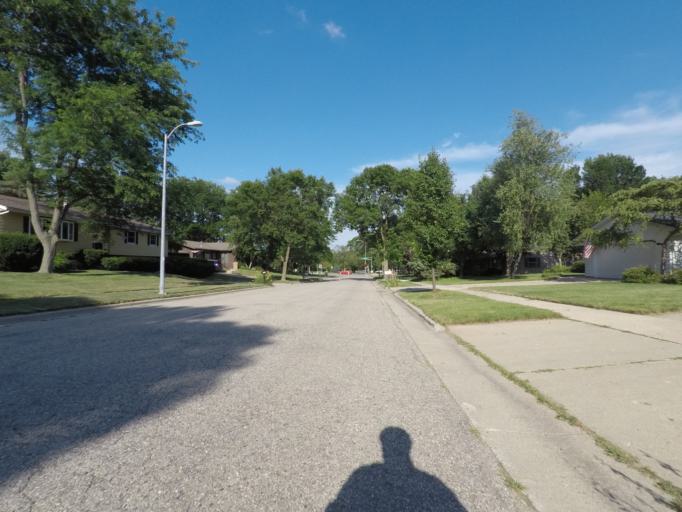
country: US
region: Wisconsin
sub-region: Dane County
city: Middleton
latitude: 43.0683
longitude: -89.5039
